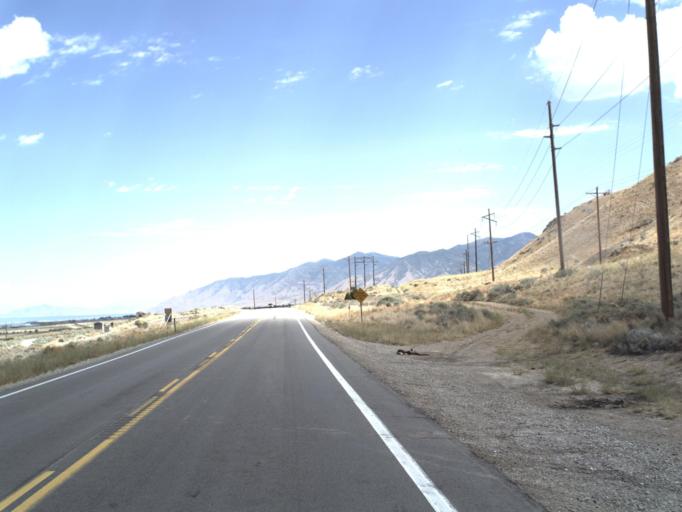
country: US
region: Utah
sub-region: Tooele County
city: Tooele
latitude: 40.4716
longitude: -112.3504
